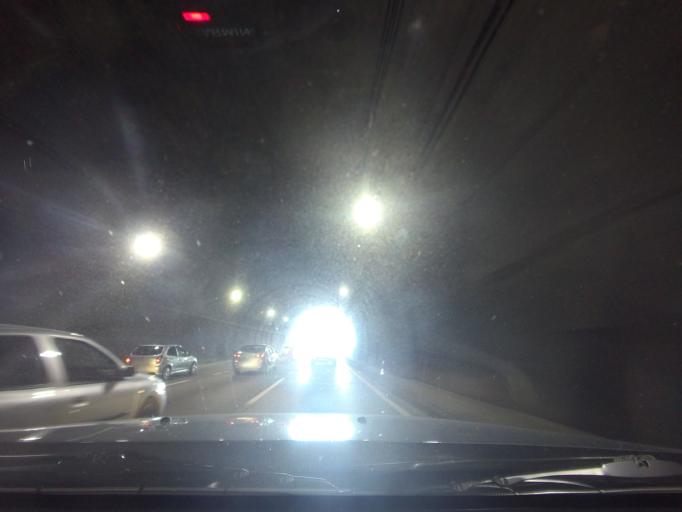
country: BR
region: Sao Paulo
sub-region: Cubatao
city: Cubatao
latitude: -23.9068
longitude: -46.5045
